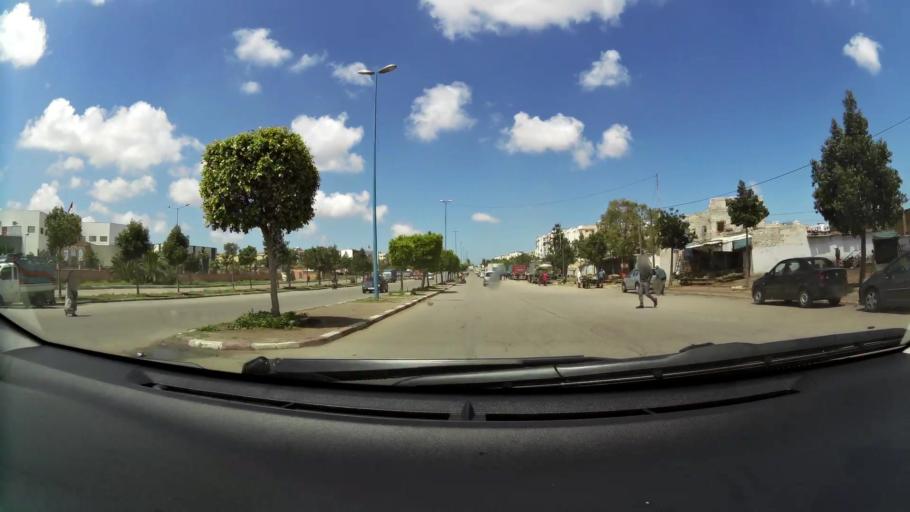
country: MA
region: Grand Casablanca
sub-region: Mediouna
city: Tit Mellil
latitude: 33.5492
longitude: -7.5488
